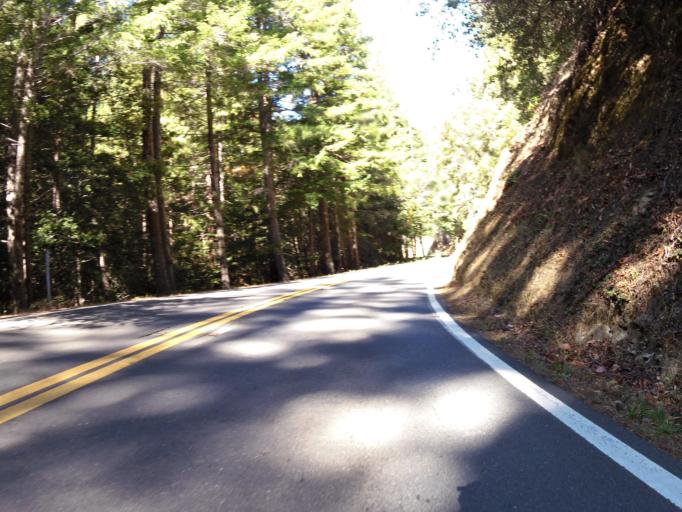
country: US
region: California
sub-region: Humboldt County
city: Redway
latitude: 39.8509
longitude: -123.7335
